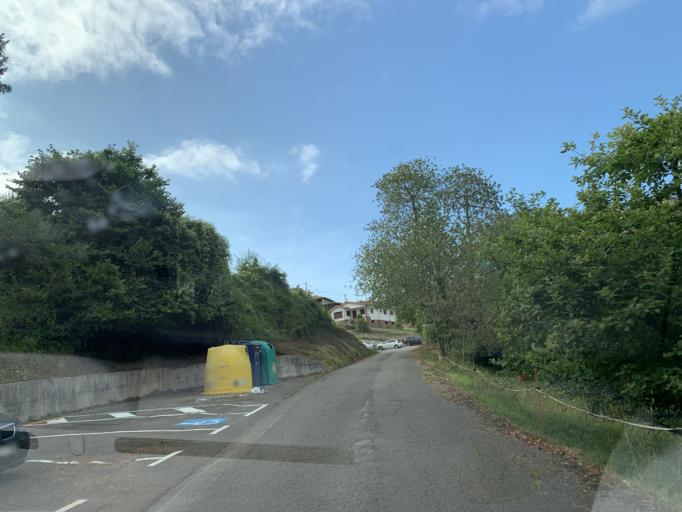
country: ES
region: Asturias
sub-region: Province of Asturias
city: Carrena
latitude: 43.3238
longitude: -4.8629
